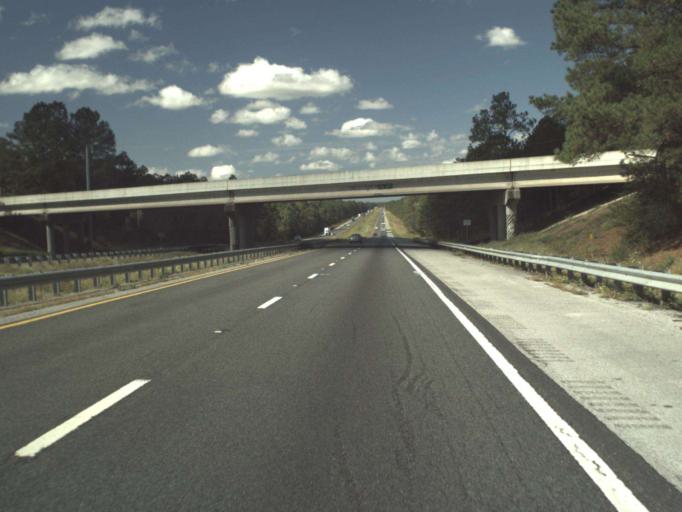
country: US
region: Florida
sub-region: Washington County
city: Chipley
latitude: 30.7522
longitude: -85.5835
